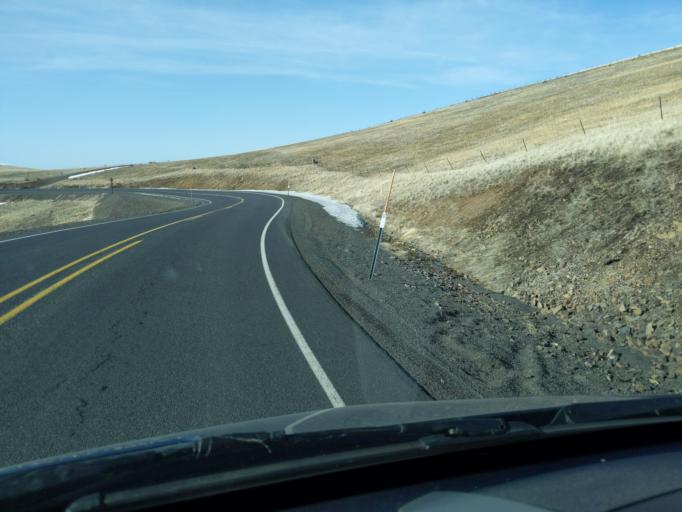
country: US
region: Oregon
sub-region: Umatilla County
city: Pilot Rock
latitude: 45.2981
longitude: -118.9857
